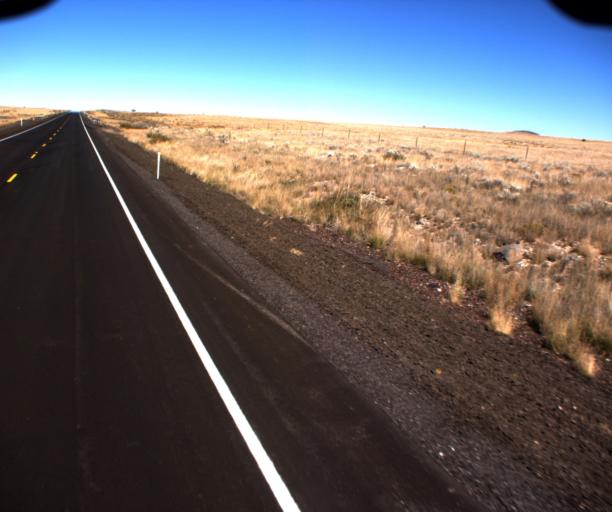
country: US
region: Arizona
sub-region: Apache County
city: Springerville
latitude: 34.2144
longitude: -109.3324
